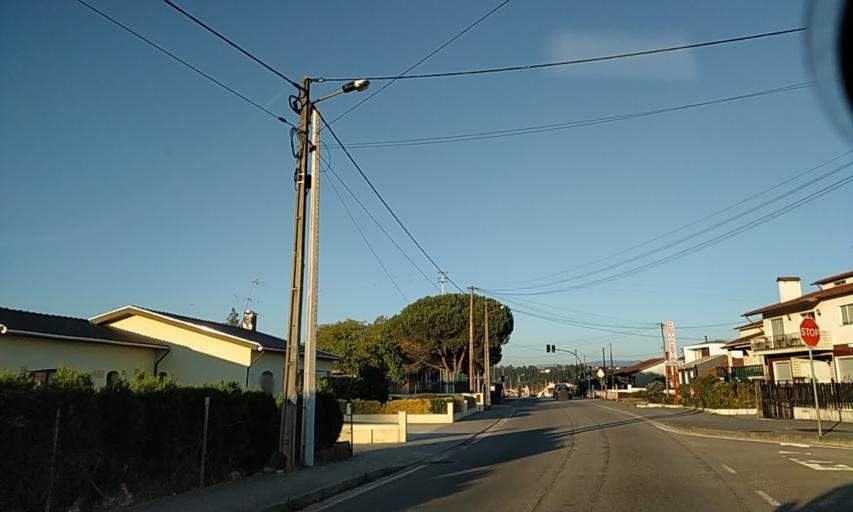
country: PT
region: Aveiro
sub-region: Oliveira do Bairro
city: Oia
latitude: 40.5456
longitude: -8.5150
